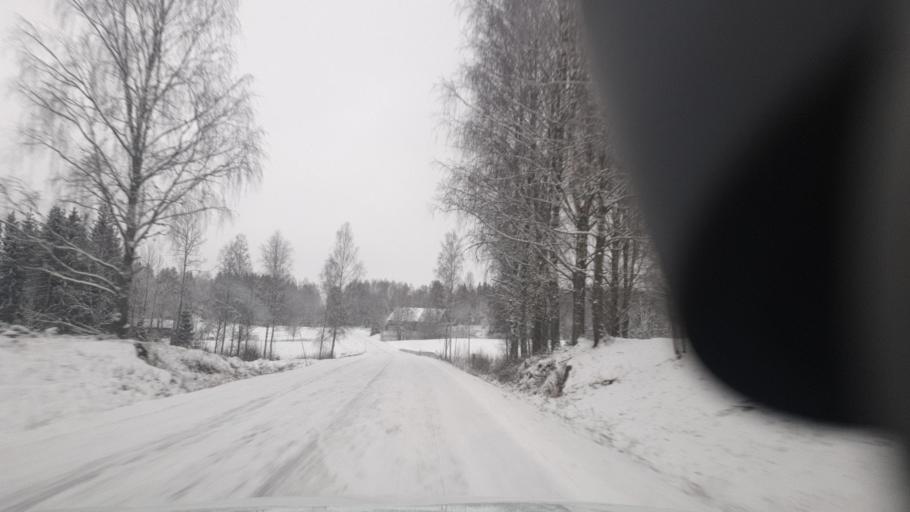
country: SE
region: Vaermland
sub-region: Eda Kommun
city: Charlottenberg
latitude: 59.7934
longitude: 12.1540
